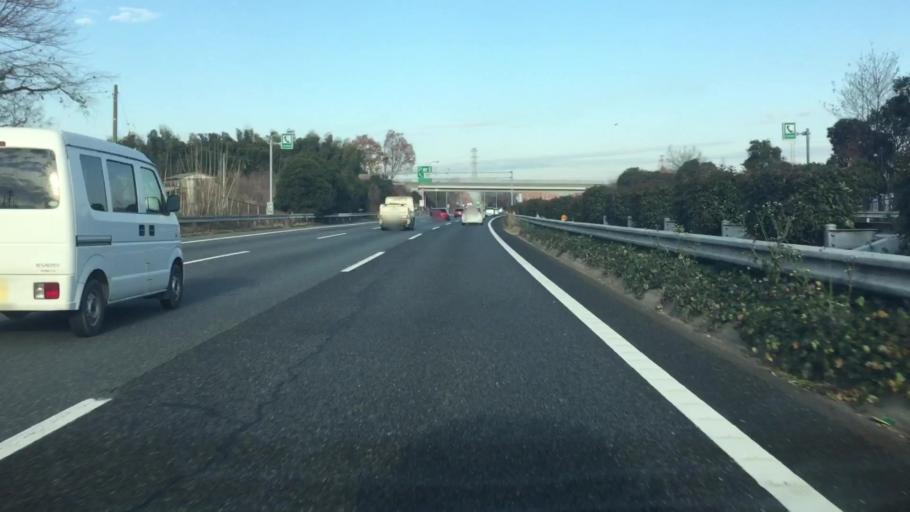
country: JP
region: Saitama
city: Yorii
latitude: 36.1686
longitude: 139.1972
